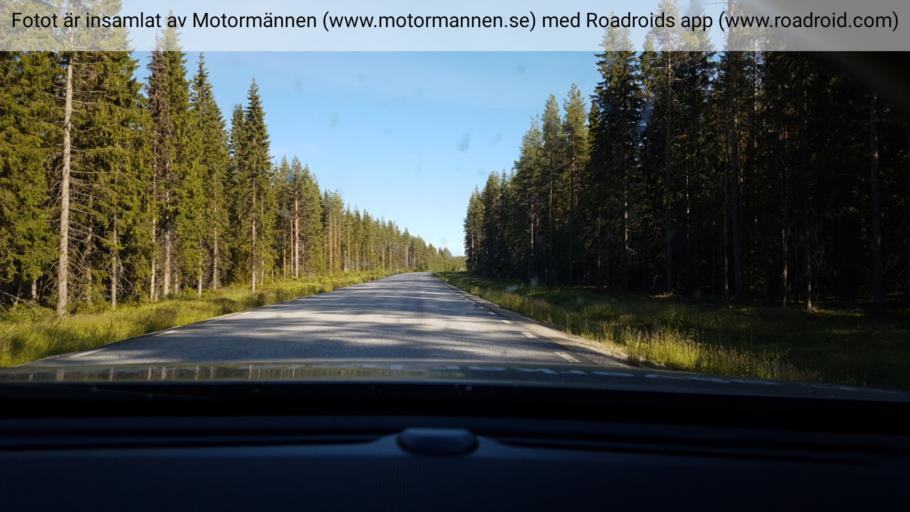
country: SE
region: Vaesterbotten
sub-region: Vindelns Kommun
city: Vindeln
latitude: 64.0910
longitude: 19.6140
